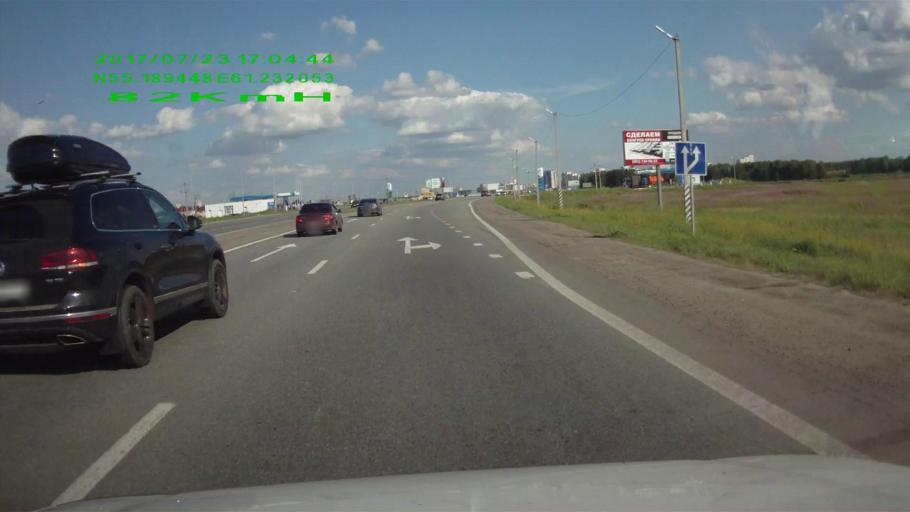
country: RU
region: Chelyabinsk
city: Roshchino
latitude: 55.1890
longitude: 61.2335
